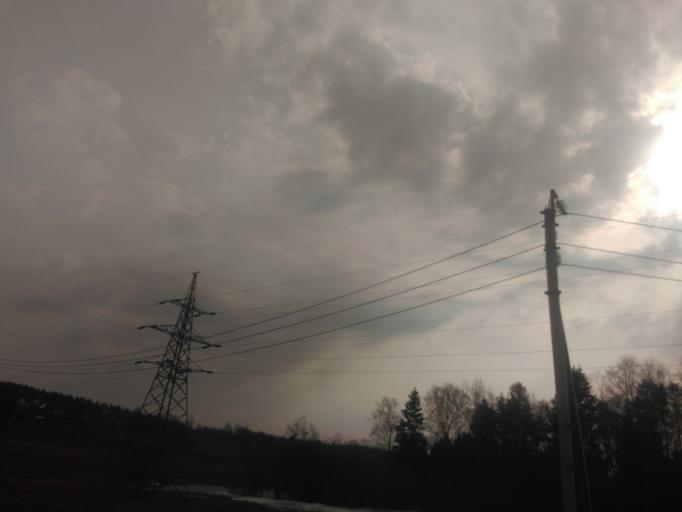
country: RU
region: Moskovskaya
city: Tuchkovo
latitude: 55.6100
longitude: 36.4202
